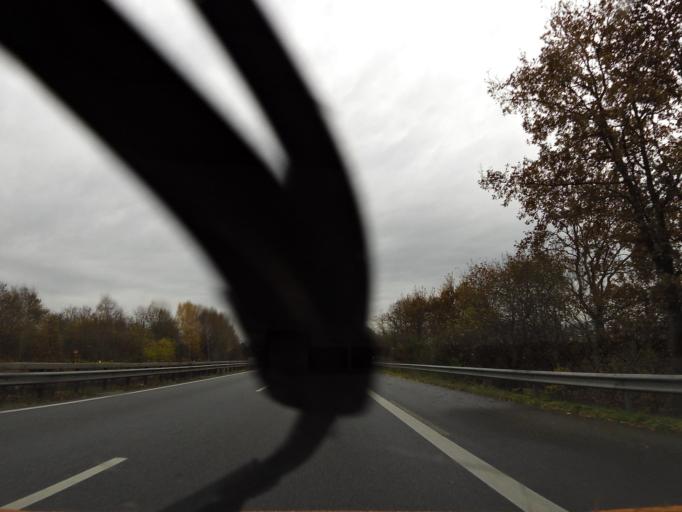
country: DE
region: Lower Saxony
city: Hatten
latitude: 53.0706
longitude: 8.3305
